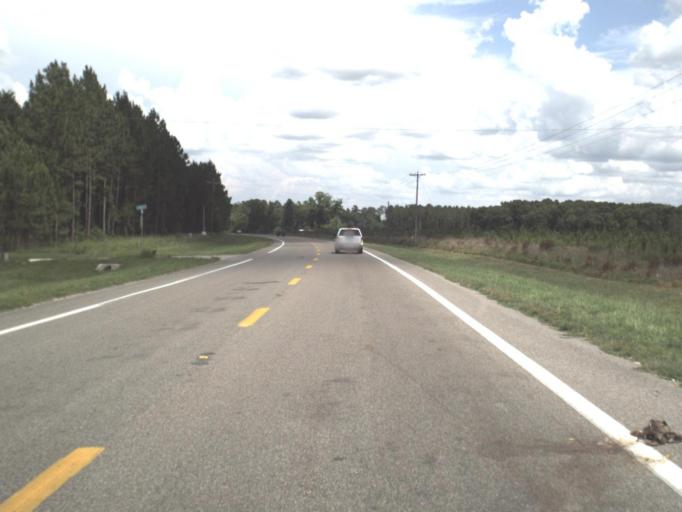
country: US
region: Florida
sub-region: Lafayette County
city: Mayo
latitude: 29.9521
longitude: -82.9568
